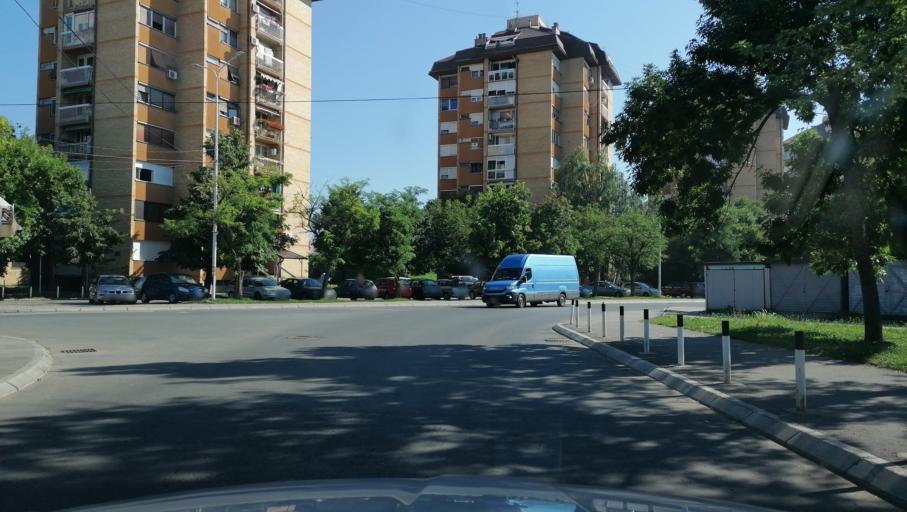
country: RS
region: Central Serbia
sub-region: Rasinski Okrug
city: Krusevac
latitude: 43.5690
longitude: 21.3344
